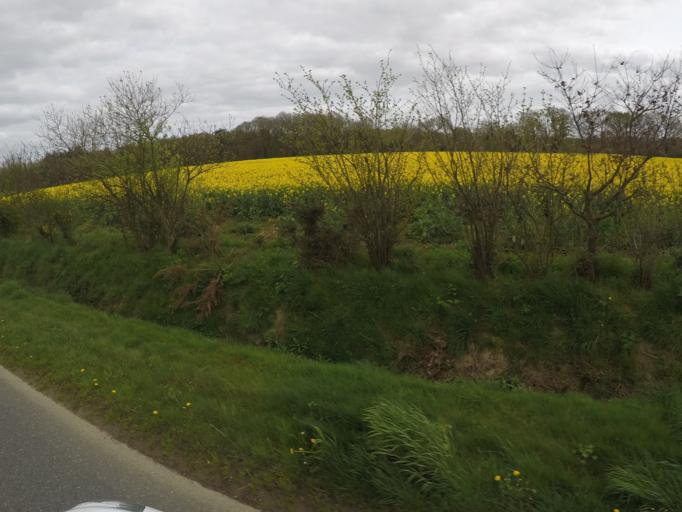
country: FR
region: Brittany
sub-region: Departement des Cotes-d'Armor
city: Pleguien
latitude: 48.6544
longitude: -2.9594
